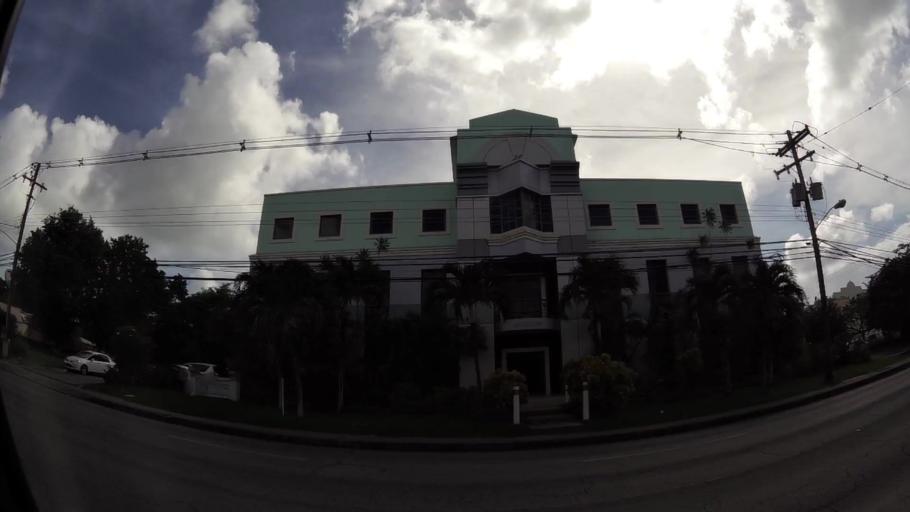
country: BB
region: Saint Michael
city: Bridgetown
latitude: 13.0932
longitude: -59.6053
